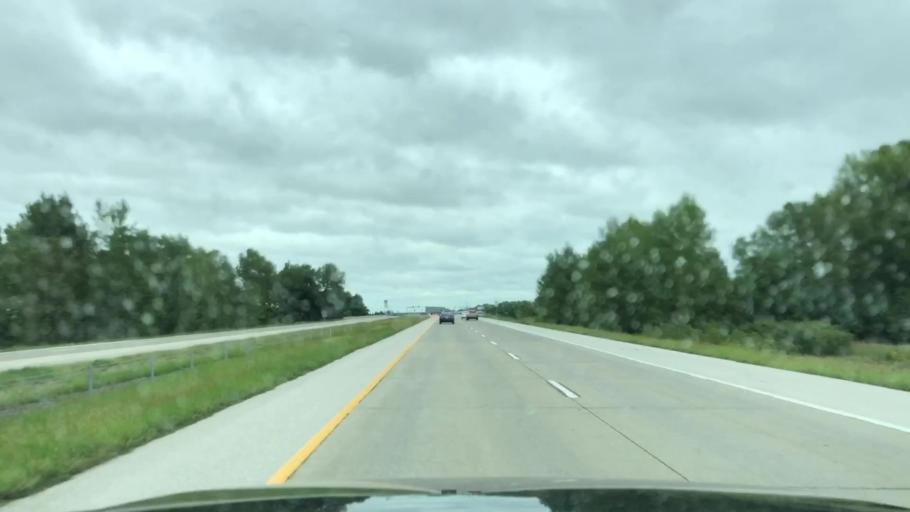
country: US
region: Missouri
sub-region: Saint Charles County
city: Saint Charles
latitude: 38.7373
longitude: -90.4774
